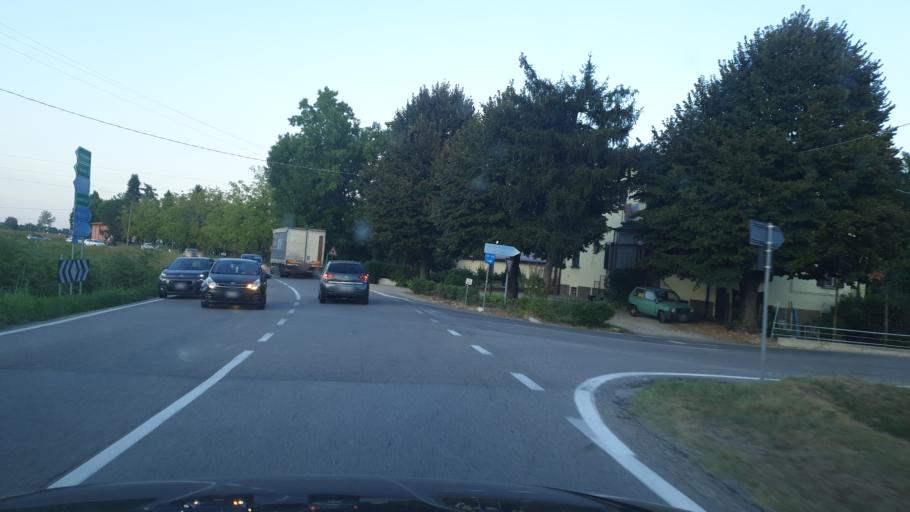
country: IT
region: Emilia-Romagna
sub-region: Provincia di Bologna
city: Progresso
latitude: 44.5641
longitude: 11.3989
